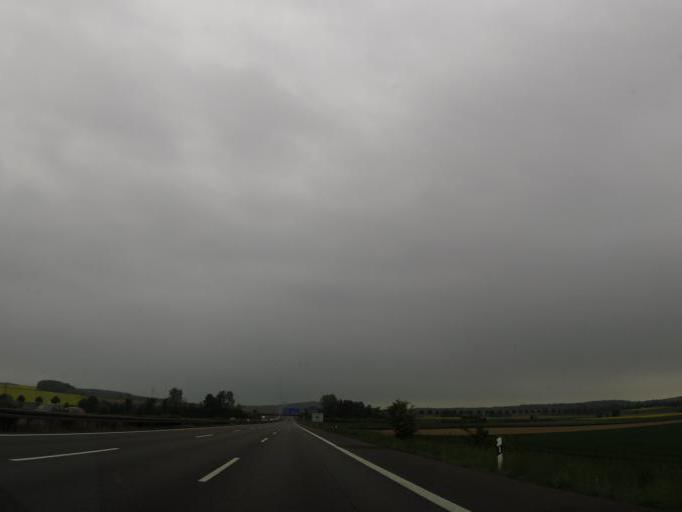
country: DE
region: Lower Saxony
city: Rosdorf
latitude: 51.4737
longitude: 9.8724
